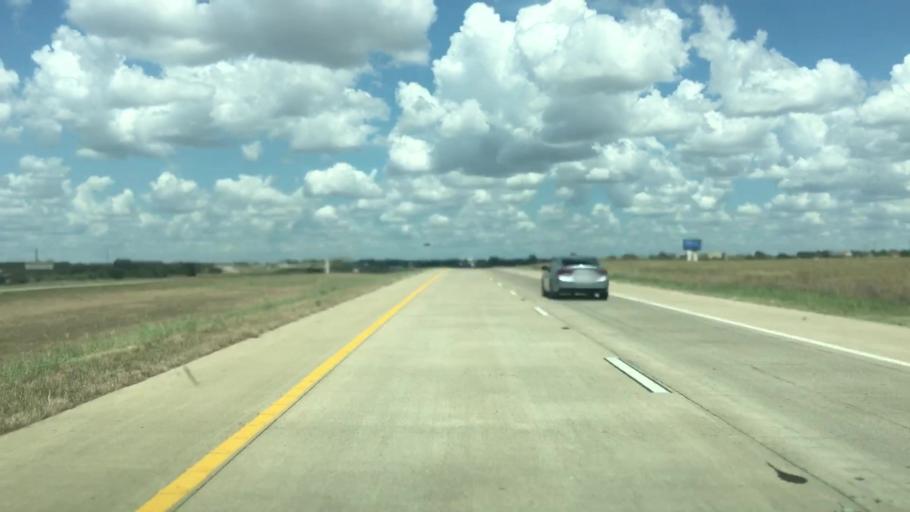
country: US
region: Texas
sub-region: Williamson County
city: Hutto
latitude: 30.5513
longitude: -97.5766
